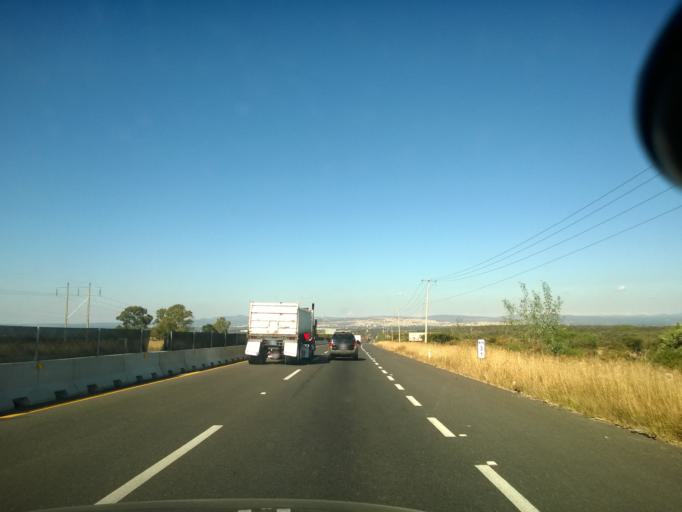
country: MX
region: Jalisco
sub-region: Lagos de Moreno
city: Geovillas Laureles del Campanario
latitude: 21.2951
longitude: -101.8626
